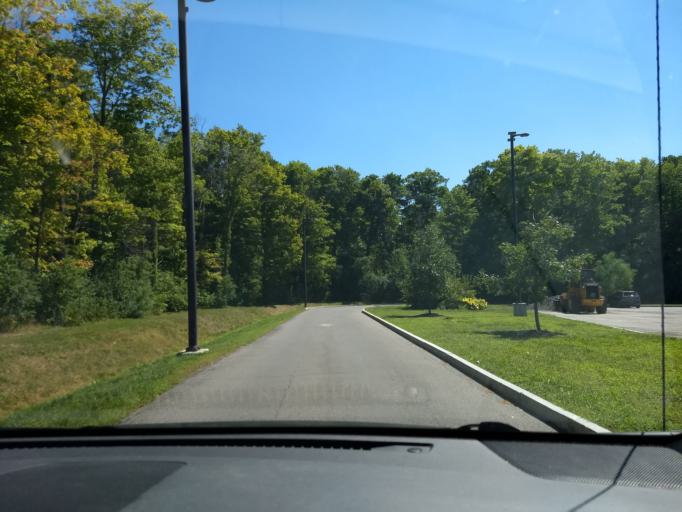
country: US
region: New York
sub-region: Niagara County
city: Niagara Falls
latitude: 43.0810
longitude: -79.0700
